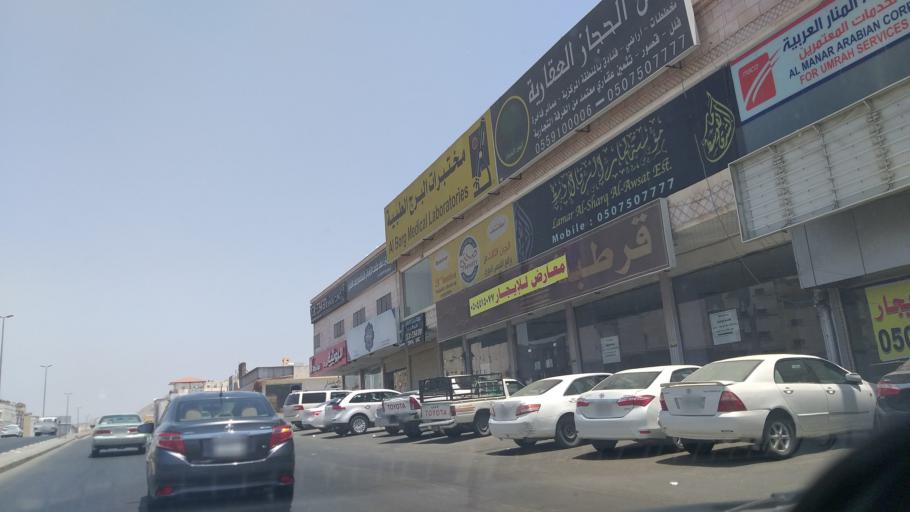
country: SA
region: Makkah
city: Mecca
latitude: 21.3760
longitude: 39.7875
